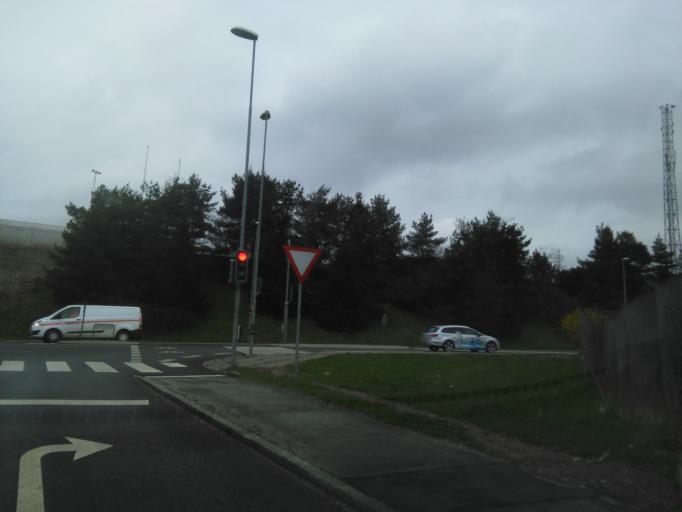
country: DK
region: Central Jutland
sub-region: Arhus Kommune
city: Stavtrup
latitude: 56.1642
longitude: 10.1010
